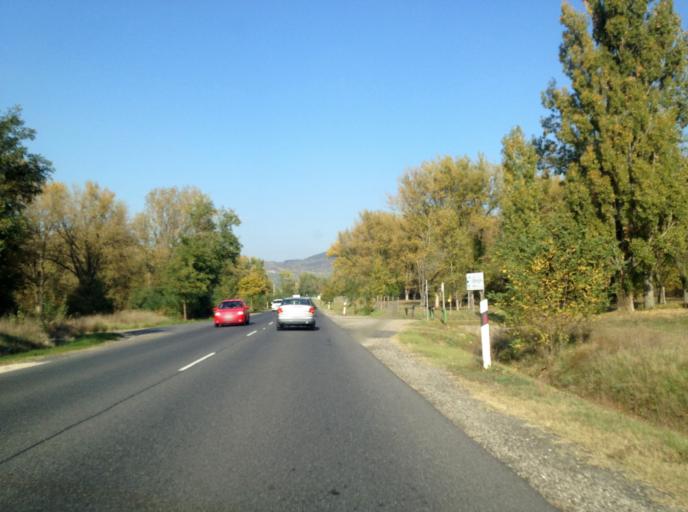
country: HU
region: Komarom-Esztergom
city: Dorog
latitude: 47.7566
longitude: 18.7418
